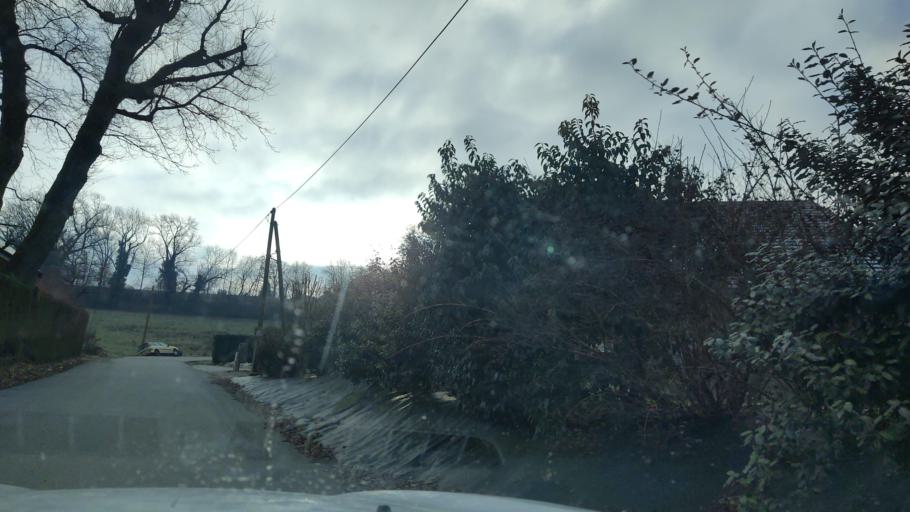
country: FR
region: Rhone-Alpes
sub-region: Departement de la Savoie
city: La Biolle
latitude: 45.7520
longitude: 5.9461
